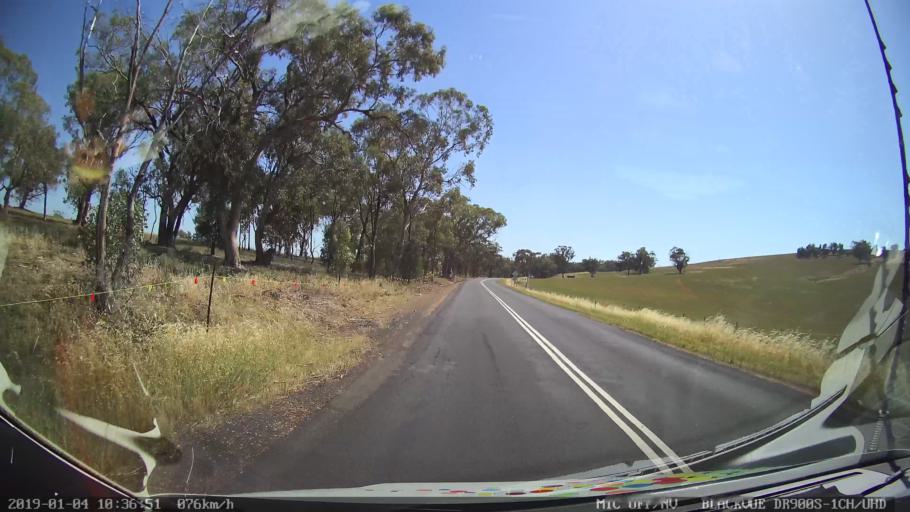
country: AU
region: New South Wales
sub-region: Cabonne
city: Canowindra
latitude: -33.3005
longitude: 148.6887
